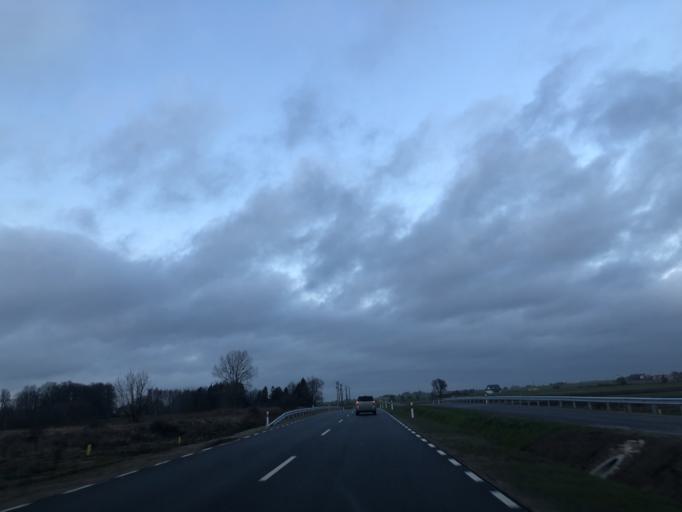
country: PL
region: Podlasie
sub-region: Lomza
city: Lomza
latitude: 53.1331
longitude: 22.0495
